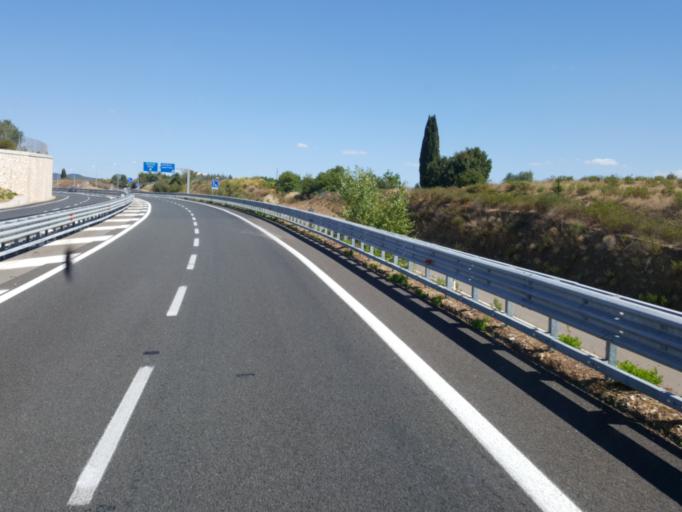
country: IT
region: Tuscany
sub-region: Provincia di Grosseto
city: Civitella Marittima
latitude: 42.9922
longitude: 11.2893
